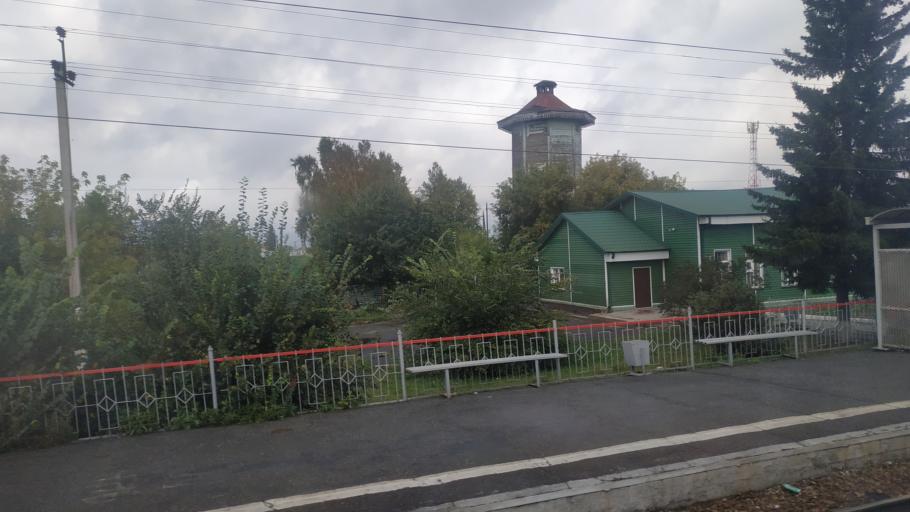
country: RU
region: Novosibirsk
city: Stantsionno-Oyashinskiy
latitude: 55.4620
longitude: 83.8197
